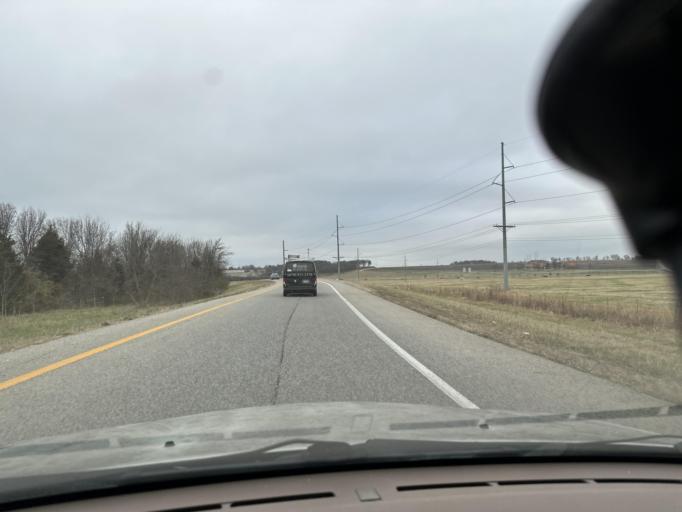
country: US
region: Arkansas
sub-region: Washington County
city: Johnson
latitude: 36.1109
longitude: -94.1686
